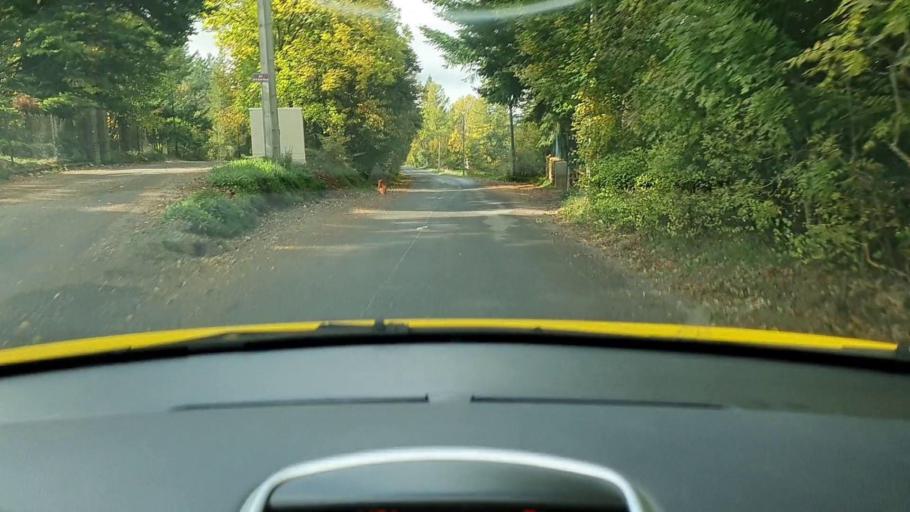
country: FR
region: Languedoc-Roussillon
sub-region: Departement de la Lozere
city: Meyrueis
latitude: 44.1141
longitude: 3.4722
